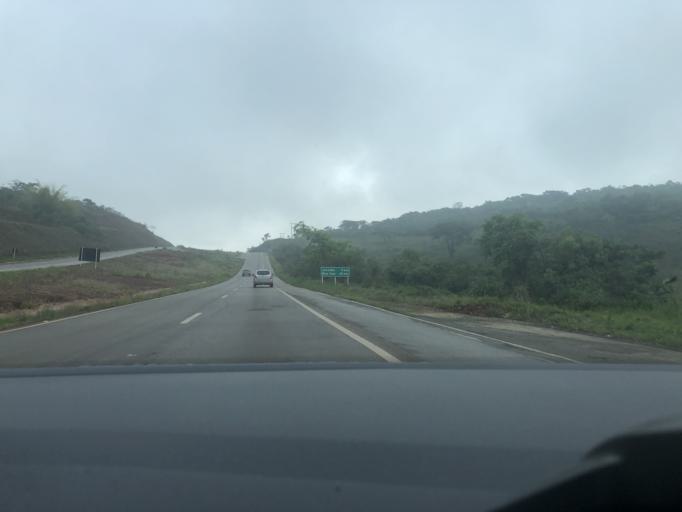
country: BR
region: Minas Gerais
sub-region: Congonhas
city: Congonhas
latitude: -20.5947
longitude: -43.9402
